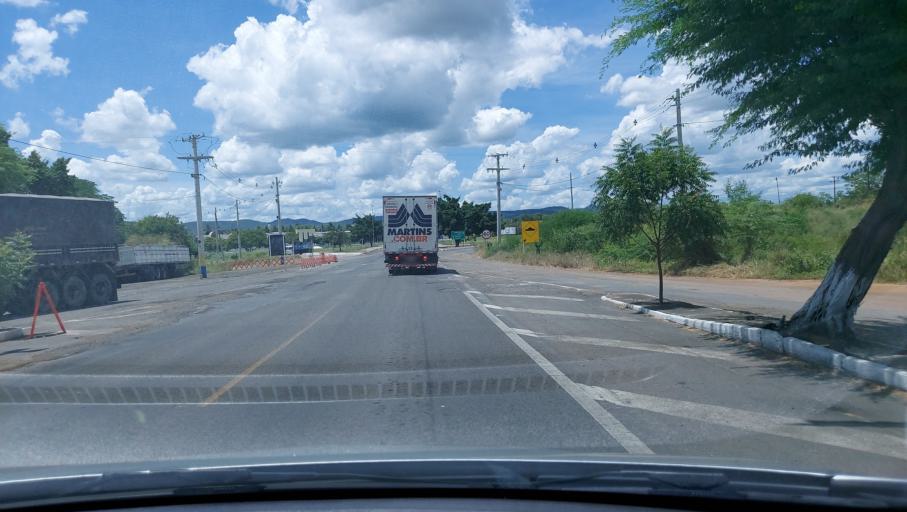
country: BR
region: Bahia
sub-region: Itaberaba
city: Itaberaba
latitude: -12.5199
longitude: -40.2797
